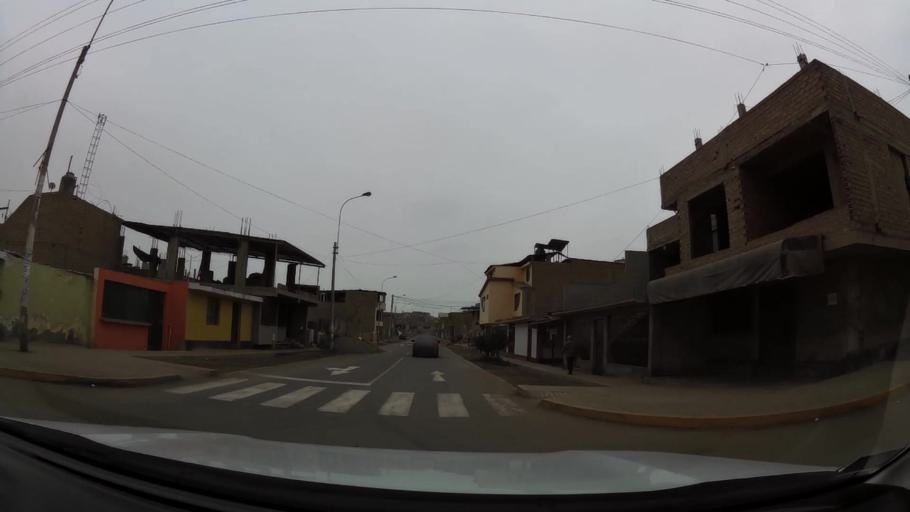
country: PE
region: Lima
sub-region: Lima
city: Surco
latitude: -12.2180
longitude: -76.9100
